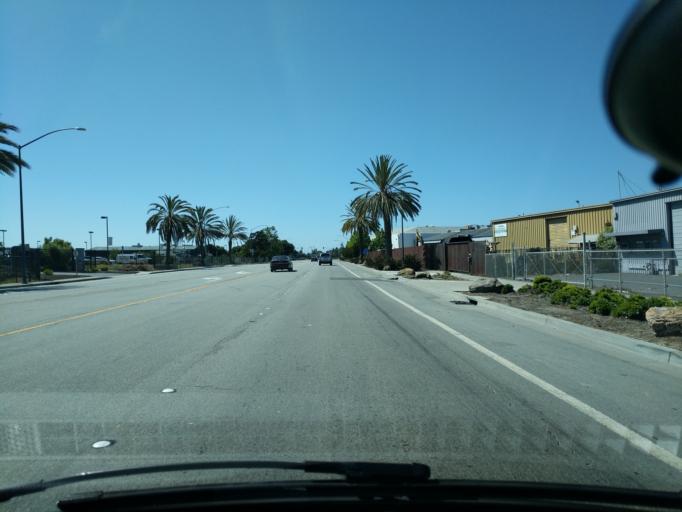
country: US
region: California
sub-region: Alameda County
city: San Leandro
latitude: 37.7203
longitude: -122.1919
